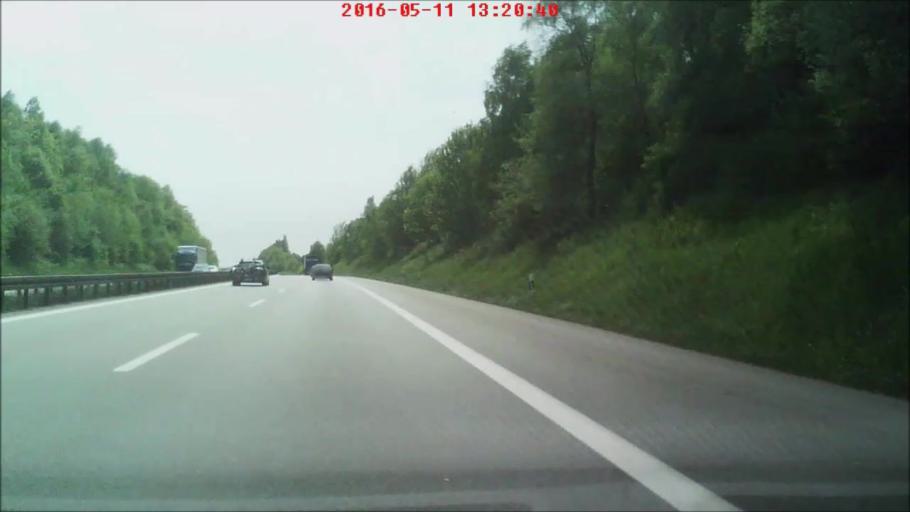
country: DE
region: Bavaria
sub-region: Lower Bavaria
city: Furstenzell
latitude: 48.4945
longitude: 13.3765
